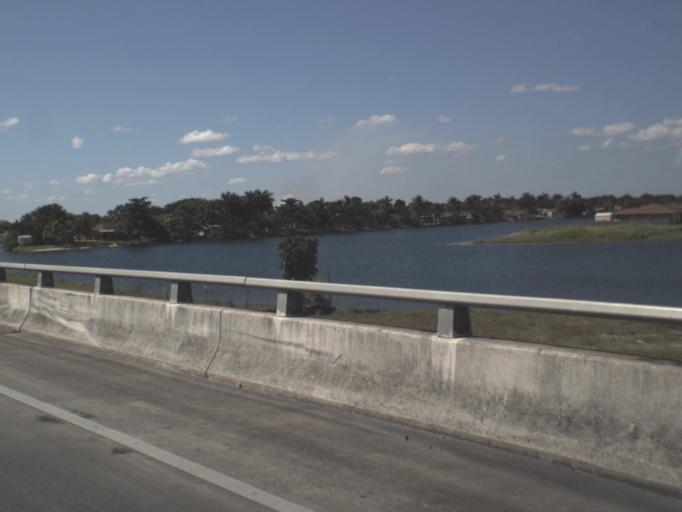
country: US
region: Florida
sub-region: Miami-Dade County
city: Leisure City
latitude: 25.4945
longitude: -80.4185
